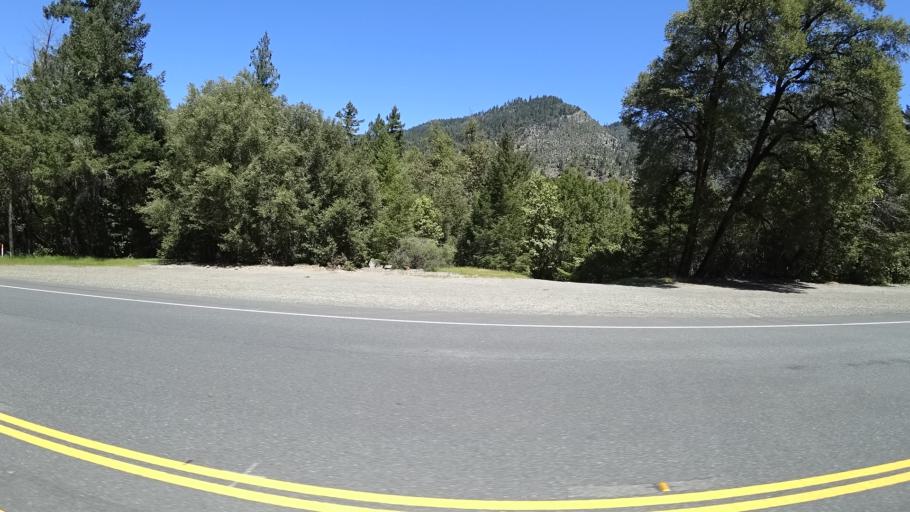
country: US
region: California
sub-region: Humboldt County
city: Willow Creek
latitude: 40.8583
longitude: -123.4966
